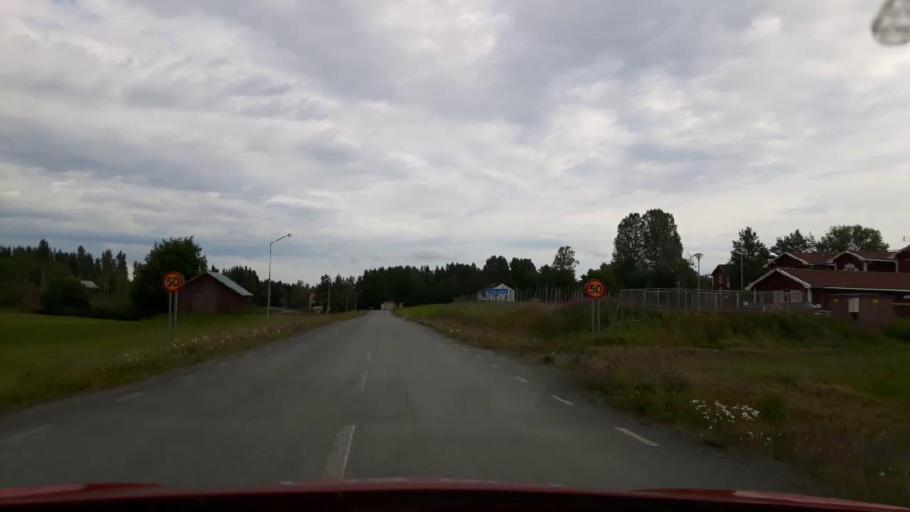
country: SE
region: Jaemtland
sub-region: OEstersunds Kommun
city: Lit
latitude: 63.4148
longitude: 15.2470
